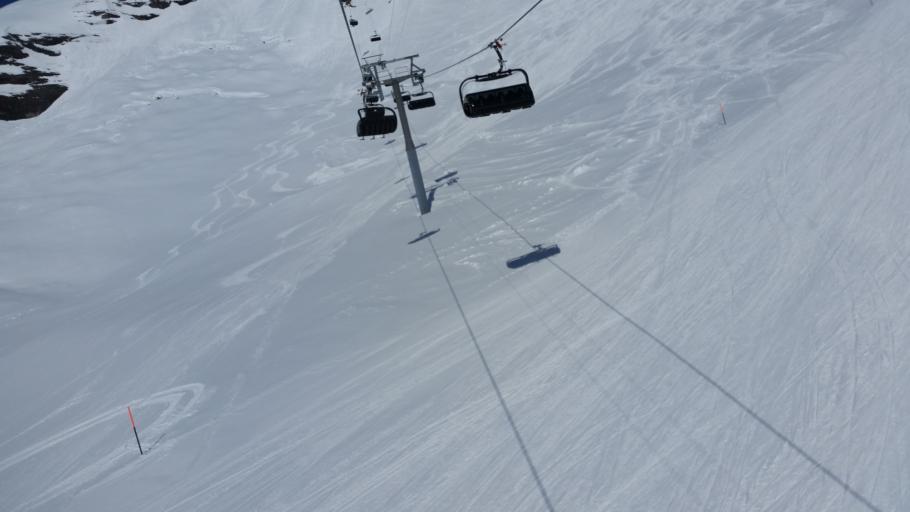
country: CH
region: Grisons
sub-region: Surselva District
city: Ilanz
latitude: 46.8440
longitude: 9.1571
